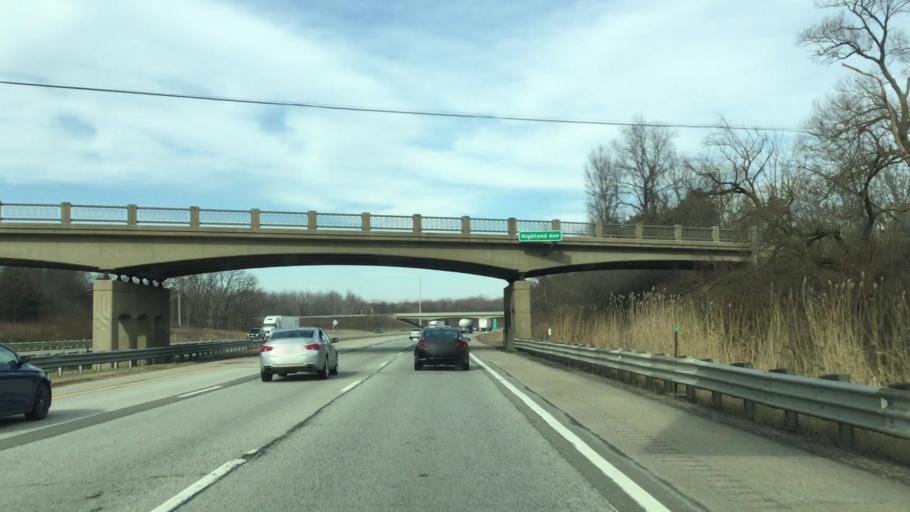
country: US
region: Michigan
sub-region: Berrien County
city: Benton Heights
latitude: 42.1156
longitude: -86.3934
